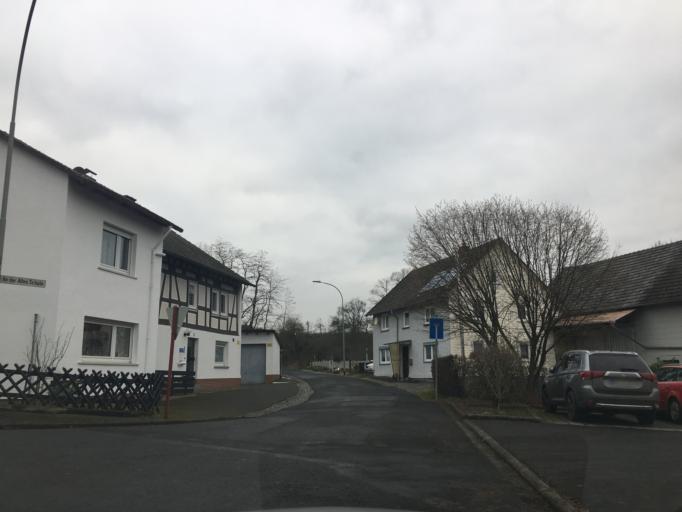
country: DE
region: Hesse
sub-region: Regierungsbezirk Giessen
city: Alsfeld
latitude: 50.6961
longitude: 9.3236
